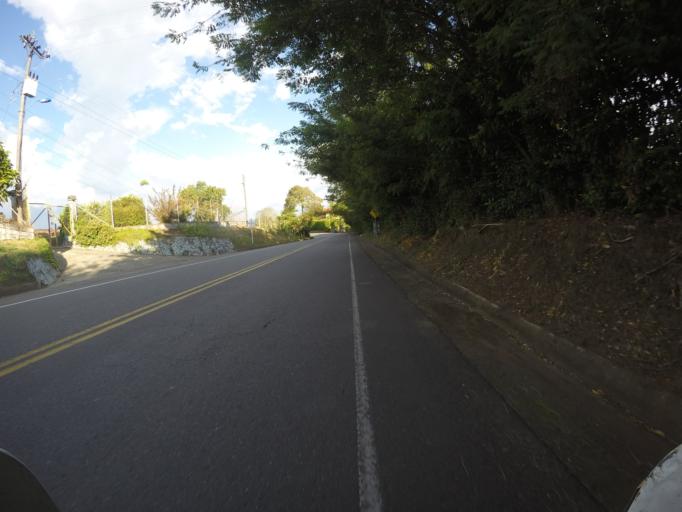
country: CO
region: Valle del Cauca
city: Alcala
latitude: 4.6930
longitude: -75.8239
